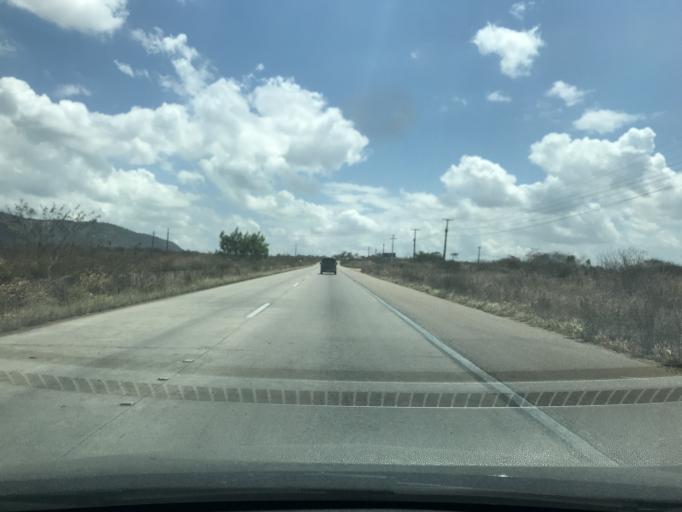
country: BR
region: Pernambuco
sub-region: Bezerros
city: Bezerros
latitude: -8.2941
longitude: -35.8262
